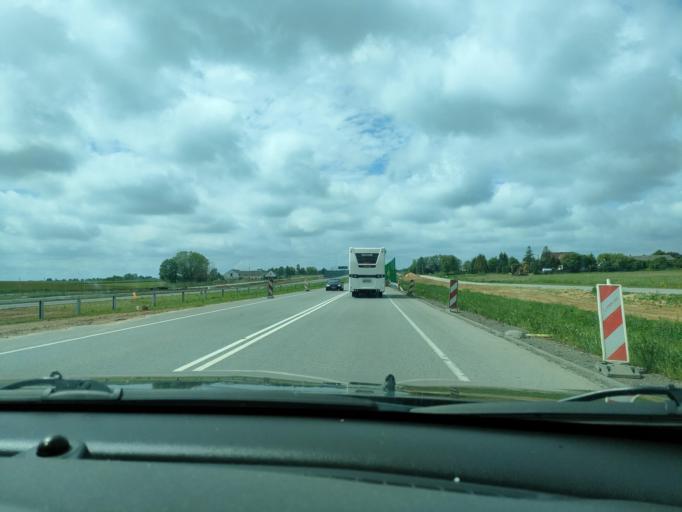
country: PL
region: Kujawsko-Pomorskie
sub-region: Powiat swiecki
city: Pruszcz
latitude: 53.3042
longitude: 18.2488
